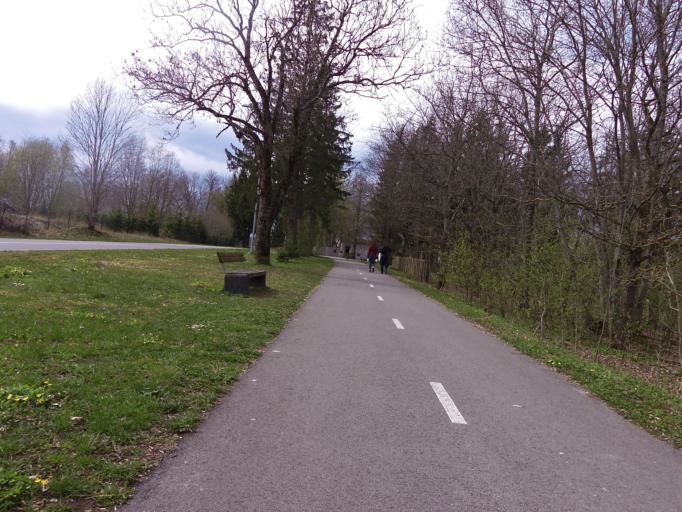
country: EE
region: Harju
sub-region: Rae vald
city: Jueri
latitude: 59.3700
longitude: 24.8331
